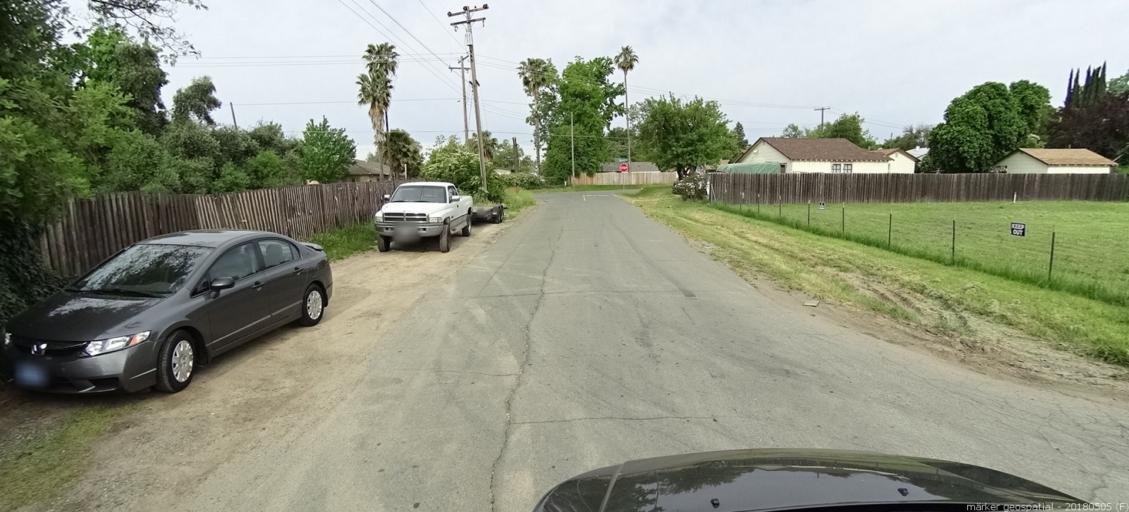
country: US
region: California
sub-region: Sacramento County
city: Rio Linda
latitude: 38.6602
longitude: -121.4449
